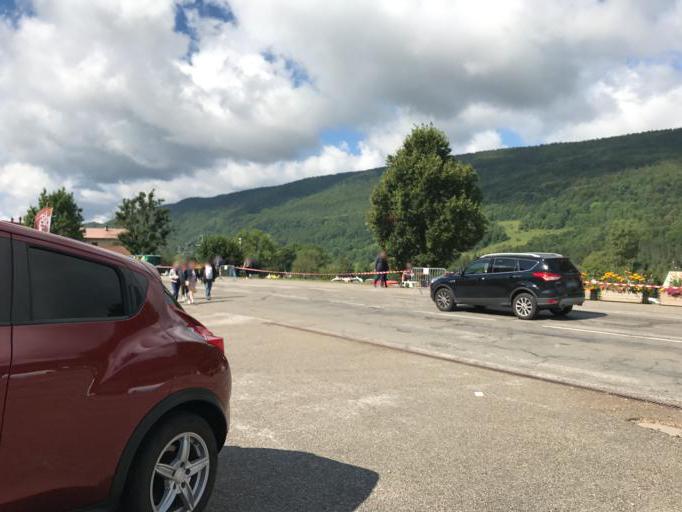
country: FR
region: Rhone-Alpes
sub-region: Departement de l'Ain
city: Sergy
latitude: 46.3065
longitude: 5.9451
